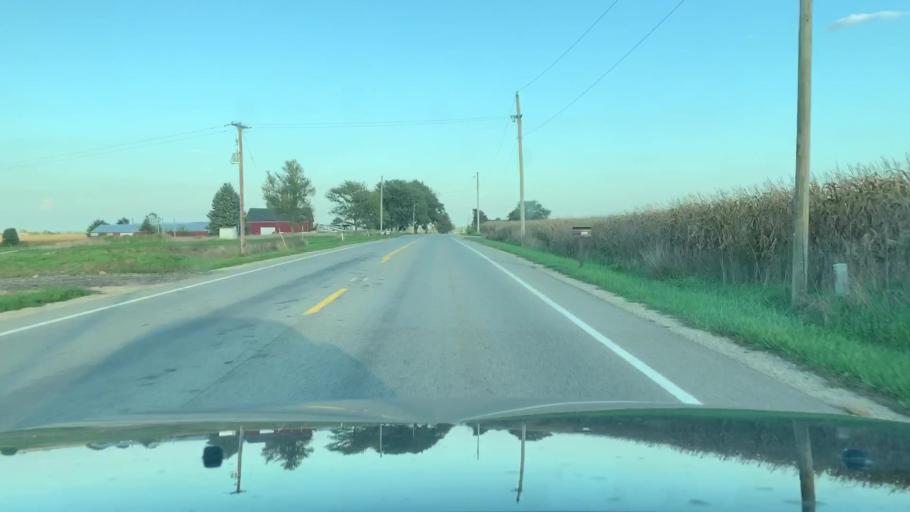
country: US
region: Michigan
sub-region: Ottawa County
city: Hudsonville
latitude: 42.8116
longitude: -85.8237
